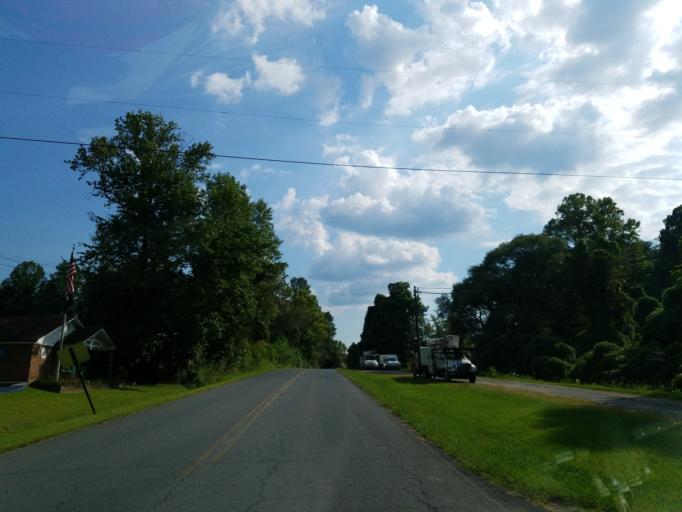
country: US
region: Georgia
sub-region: Fannin County
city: Blue Ridge
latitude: 34.7825
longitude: -84.3900
